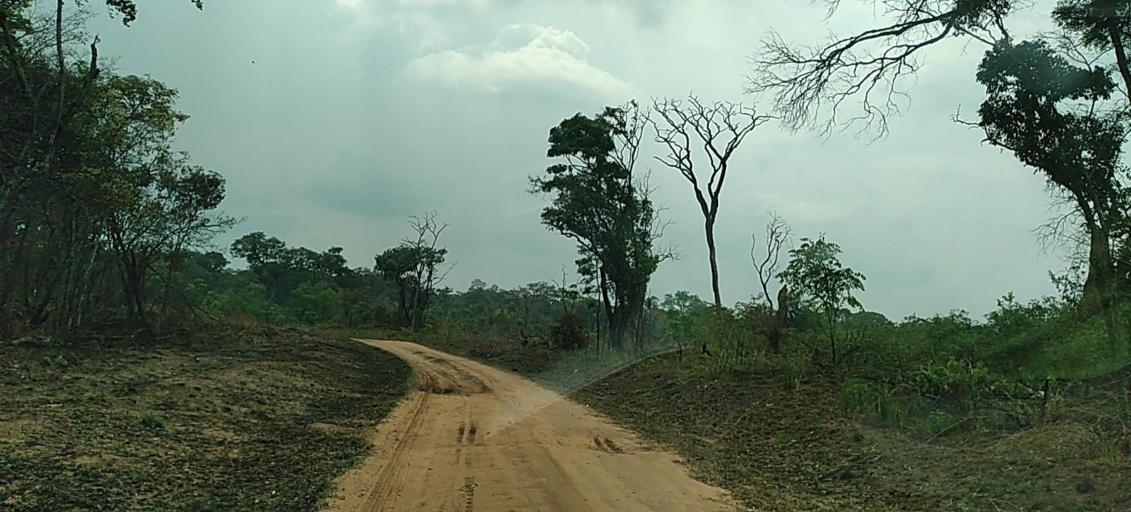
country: ZM
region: North-Western
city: Mwinilunga
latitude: -11.4665
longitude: 24.4780
